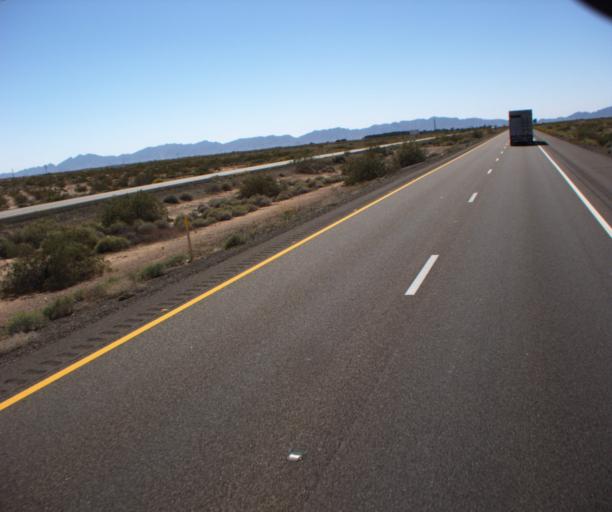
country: US
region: Arizona
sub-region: Yuma County
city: Wellton
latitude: 32.8080
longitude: -113.5220
